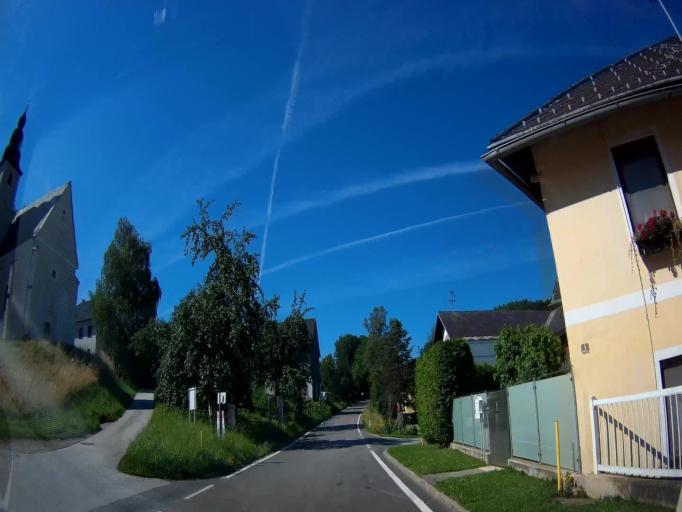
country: AT
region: Carinthia
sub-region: Politischer Bezirk Klagenfurt Land
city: Maria Saal
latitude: 46.6905
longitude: 14.3598
